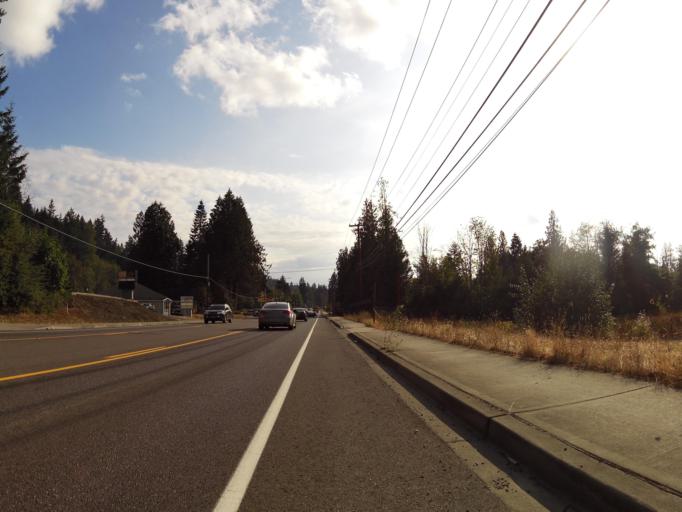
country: US
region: Washington
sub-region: Mason County
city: Belfair
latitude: 47.4430
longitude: -122.8326
